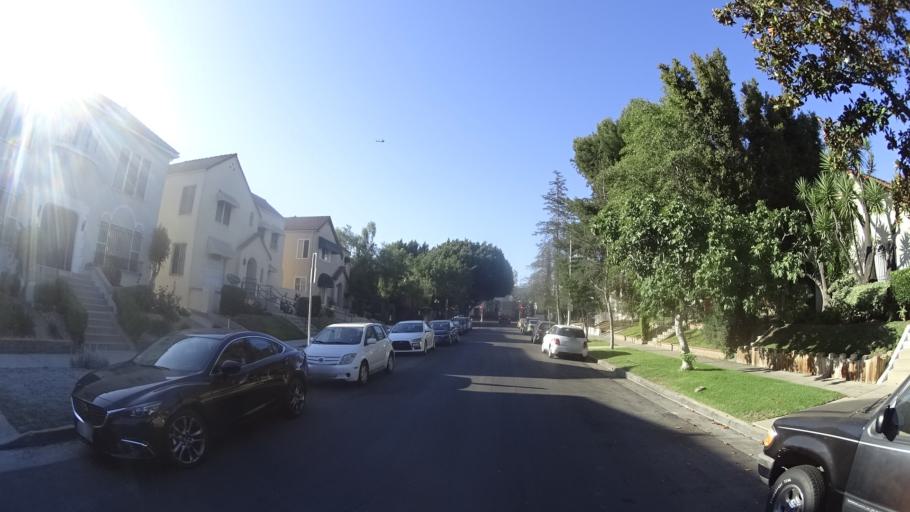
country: US
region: California
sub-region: Los Angeles County
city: Hollywood
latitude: 34.0826
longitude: -118.3207
